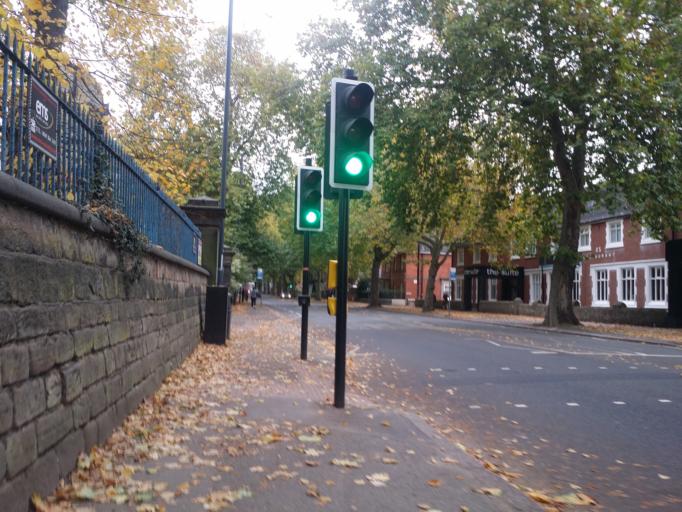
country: GB
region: England
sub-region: Derby
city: Derby
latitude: 52.9156
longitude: -1.4683
